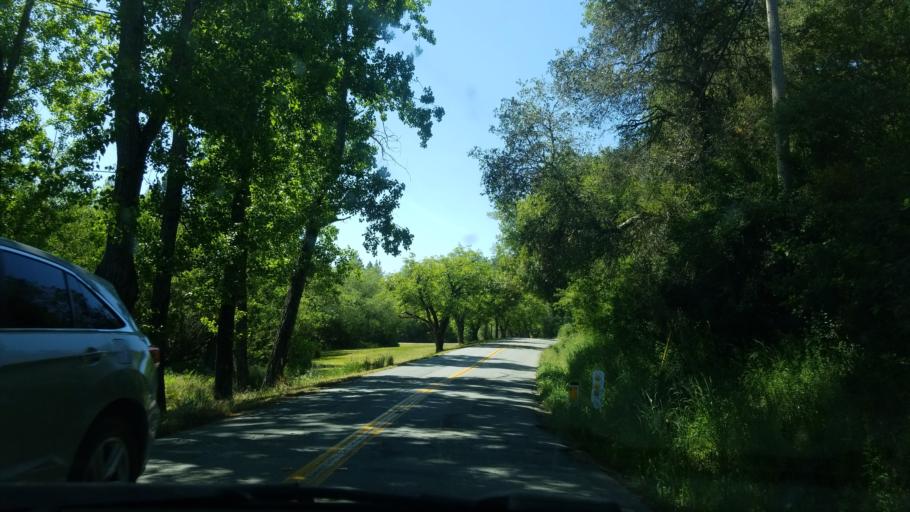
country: US
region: California
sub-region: Santa Cruz County
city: Day Valley
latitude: 37.1065
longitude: -121.9014
